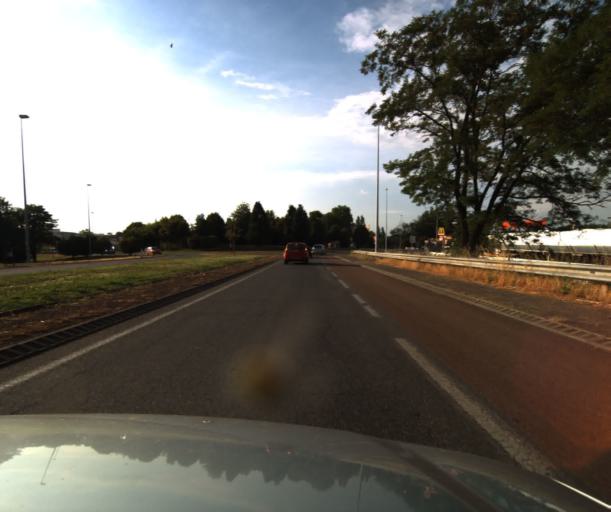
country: FR
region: Midi-Pyrenees
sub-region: Departement du Tarn-et-Garonne
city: Castelsarrasin
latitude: 44.0558
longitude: 1.0997
